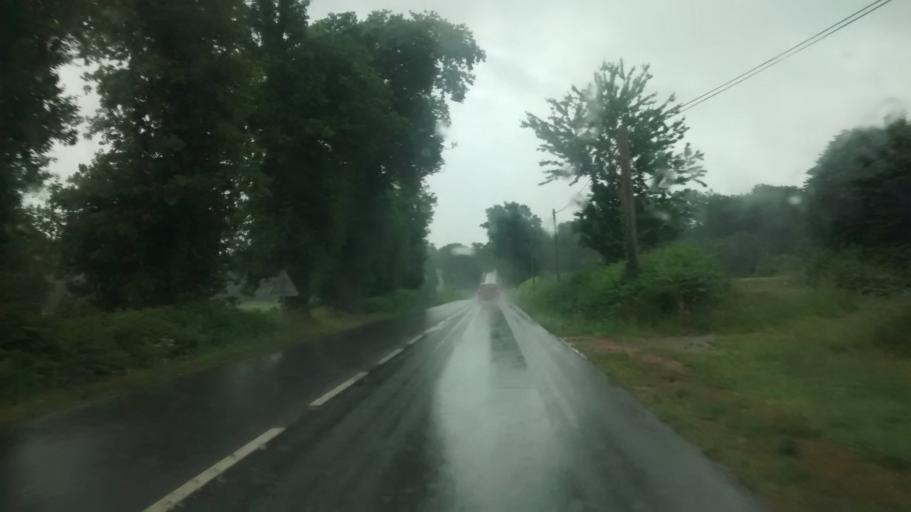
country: FR
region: Brittany
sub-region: Departement du Morbihan
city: La Gacilly
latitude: 47.7800
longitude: -2.1671
